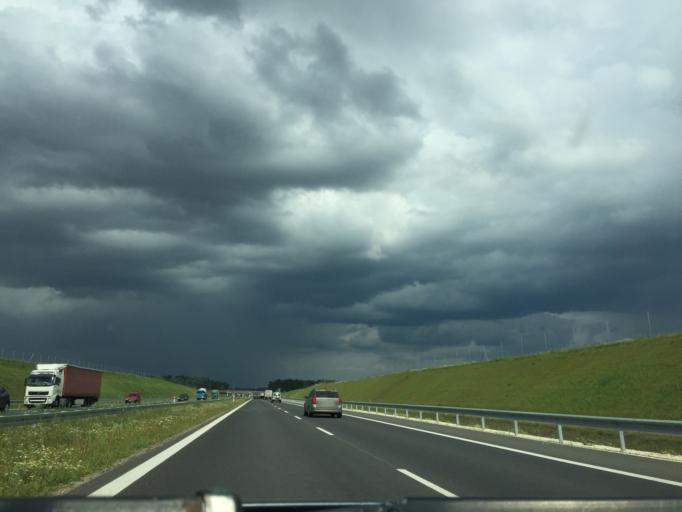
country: PL
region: Masovian Voivodeship
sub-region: Powiat szydlowiecki
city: Jastrzab
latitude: 51.2670
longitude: 20.9358
